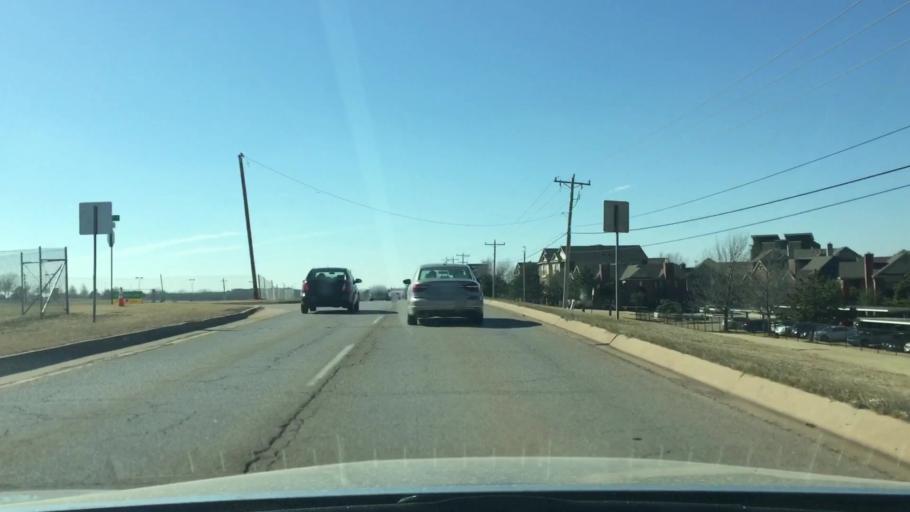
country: US
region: Oklahoma
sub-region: Oklahoma County
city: The Village
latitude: 35.6103
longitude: -97.5936
